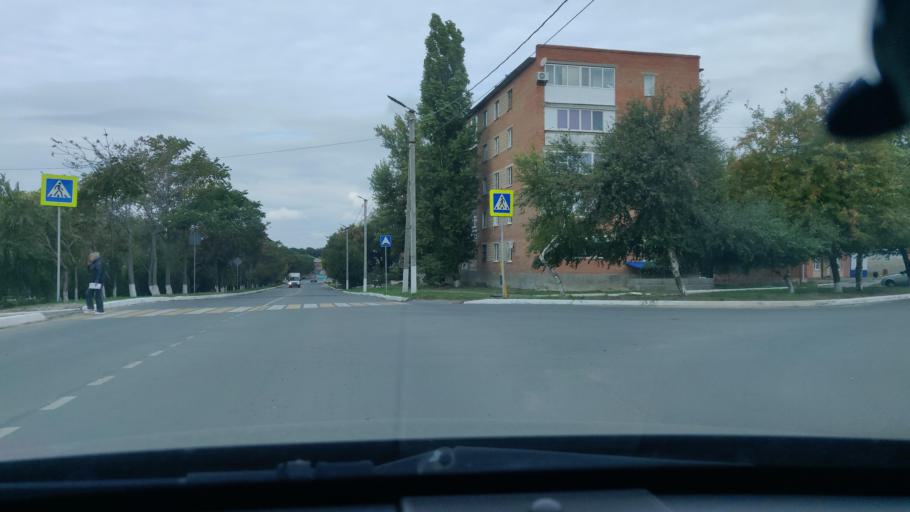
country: RU
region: Rostov
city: Ust'-Donetskiy
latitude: 47.6436
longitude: 40.8639
